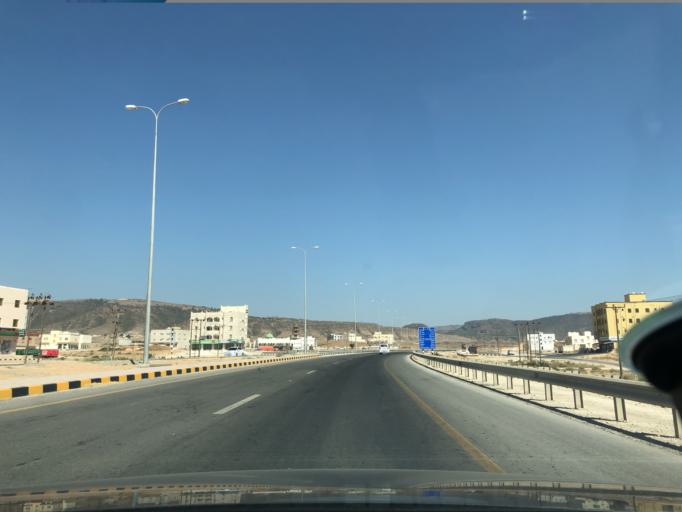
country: OM
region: Zufar
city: Salalah
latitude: 17.0507
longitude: 54.4003
